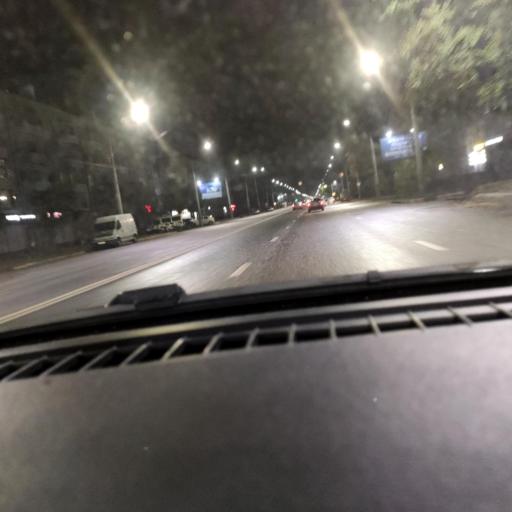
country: RU
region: Voronezj
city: Voronezh
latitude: 51.6352
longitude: 39.2335
